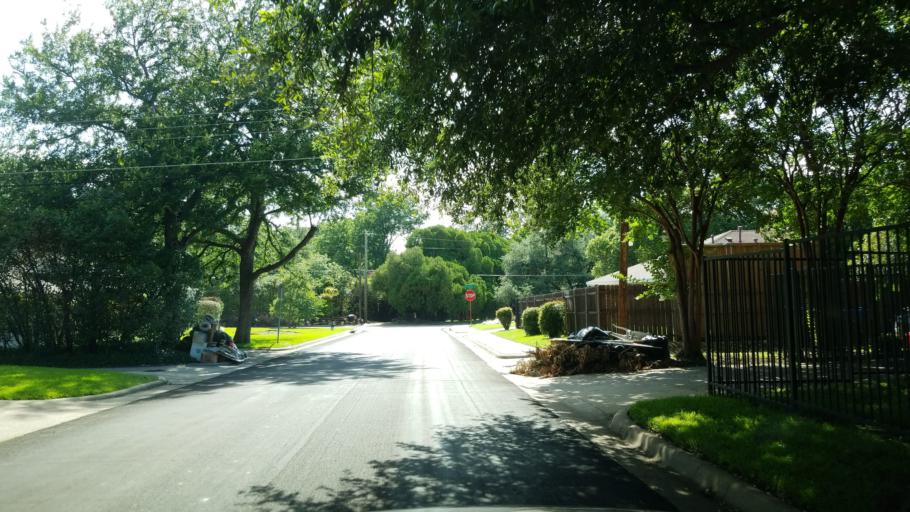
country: US
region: Texas
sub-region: Dallas County
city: University Park
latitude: 32.8835
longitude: -96.8501
